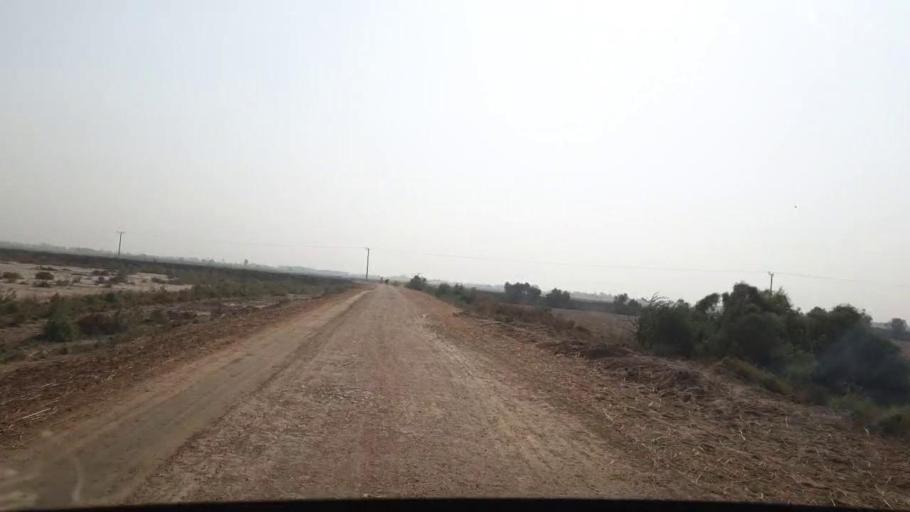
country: PK
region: Sindh
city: Chuhar Jamali
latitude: 24.3724
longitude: 67.9446
